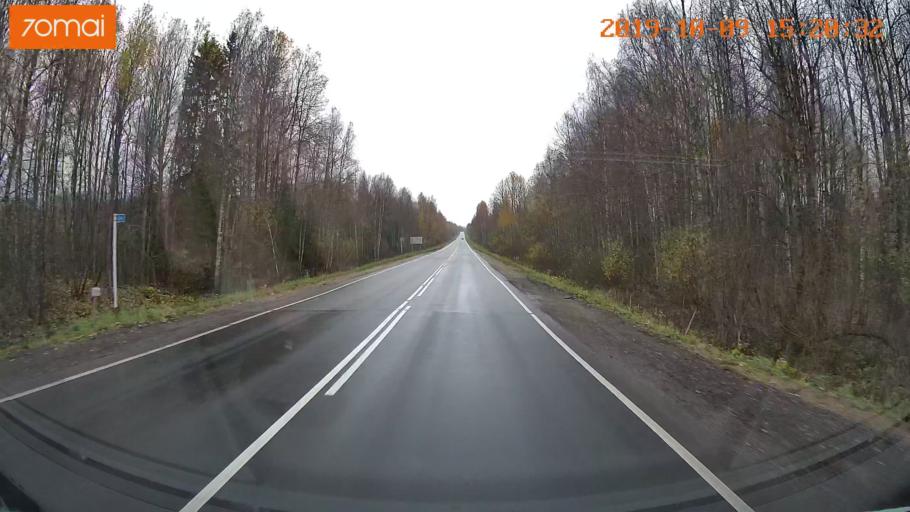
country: RU
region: Kostroma
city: Susanino
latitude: 58.0633
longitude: 41.5361
